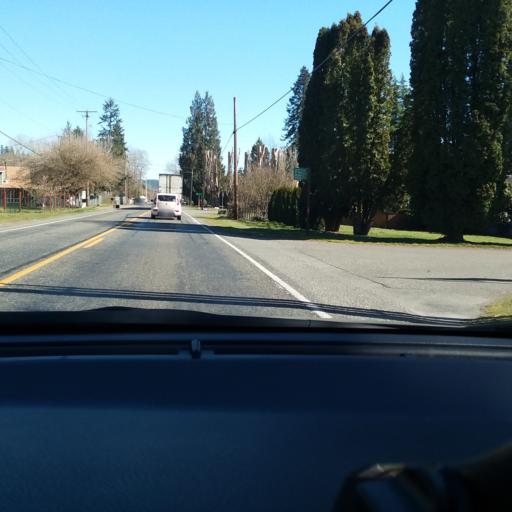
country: US
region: Washington
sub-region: Pierce County
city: North Puyallup
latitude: 47.2062
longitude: -122.2720
